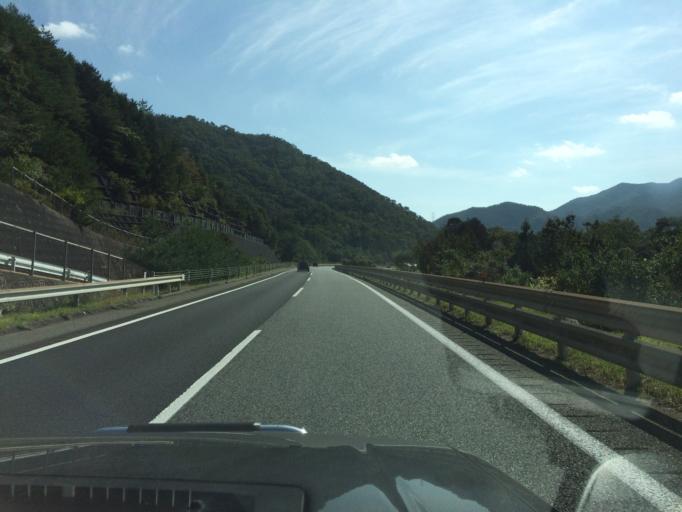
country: JP
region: Hyogo
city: Sasayama
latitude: 35.0067
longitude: 135.1593
